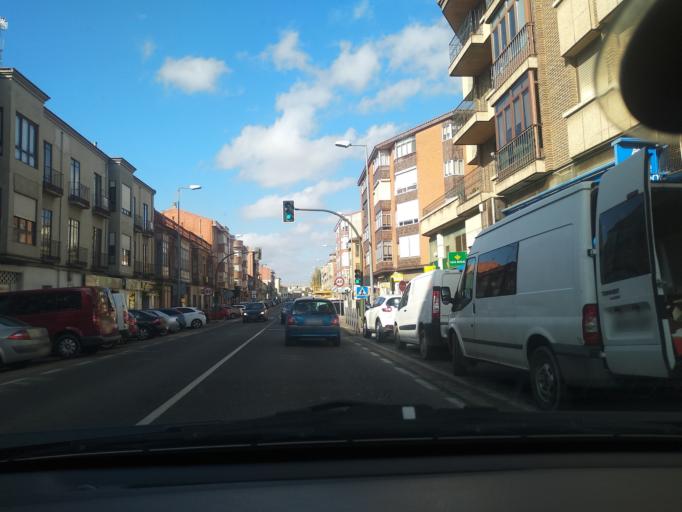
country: ES
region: Castille and Leon
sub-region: Provincia de Valladolid
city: Medina de Rioseco
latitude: 41.8836
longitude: -5.0453
